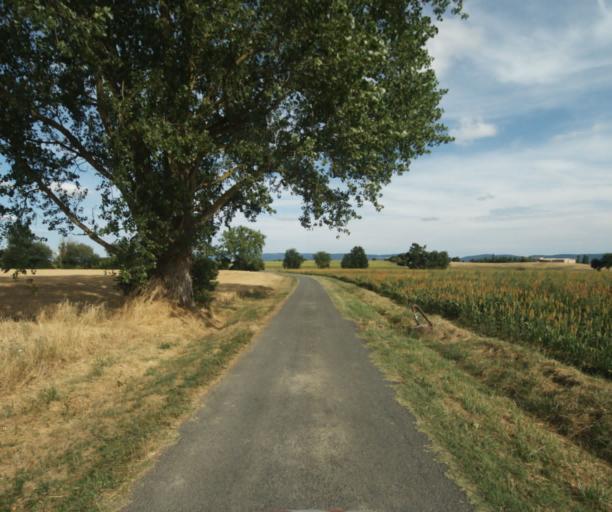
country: FR
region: Midi-Pyrenees
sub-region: Departement de la Haute-Garonne
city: Revel
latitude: 43.5151
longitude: 1.9913
